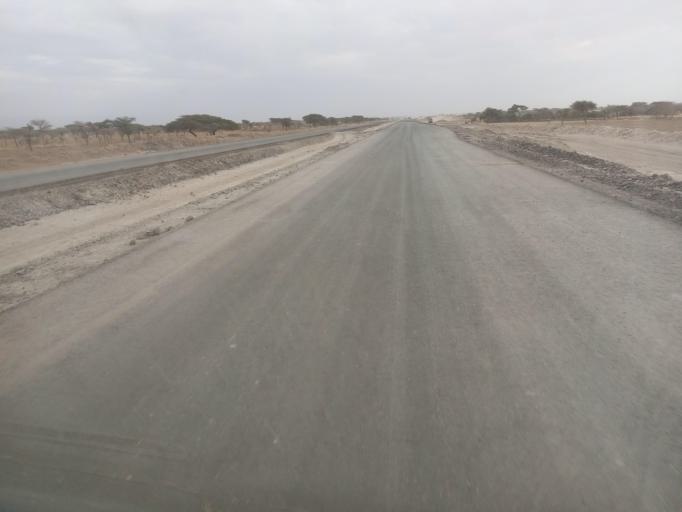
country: ET
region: Oromiya
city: Ziway
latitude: 7.7438
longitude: 38.6184
